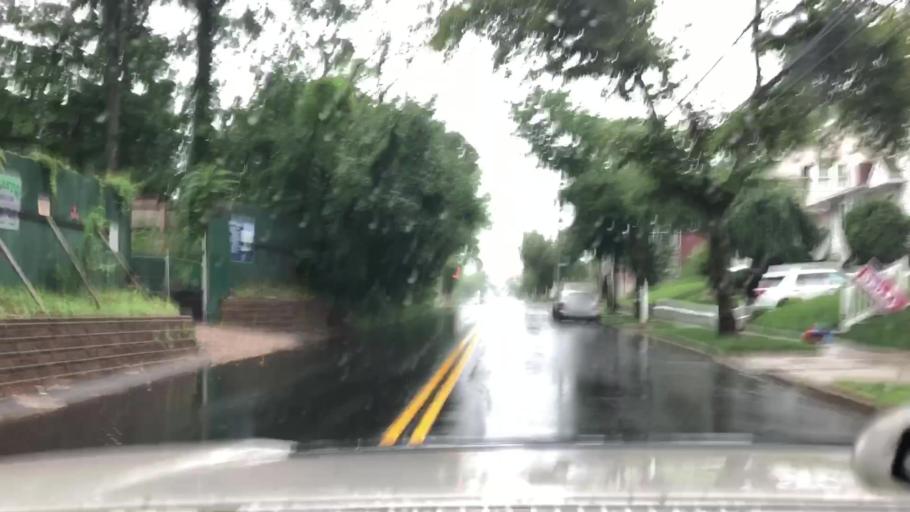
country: US
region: New Jersey
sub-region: Middlesex County
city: Carteret
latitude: 40.5380
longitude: -74.1948
